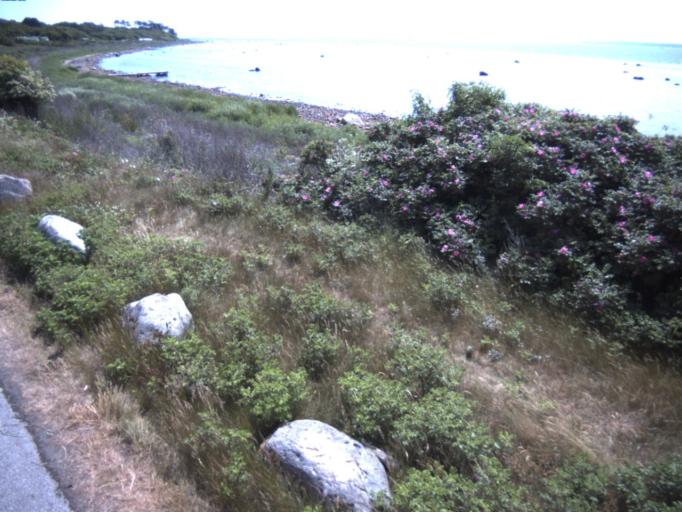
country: DK
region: Capital Region
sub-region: Helsingor Kommune
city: Hellebaek
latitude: 56.1135
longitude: 12.6125
